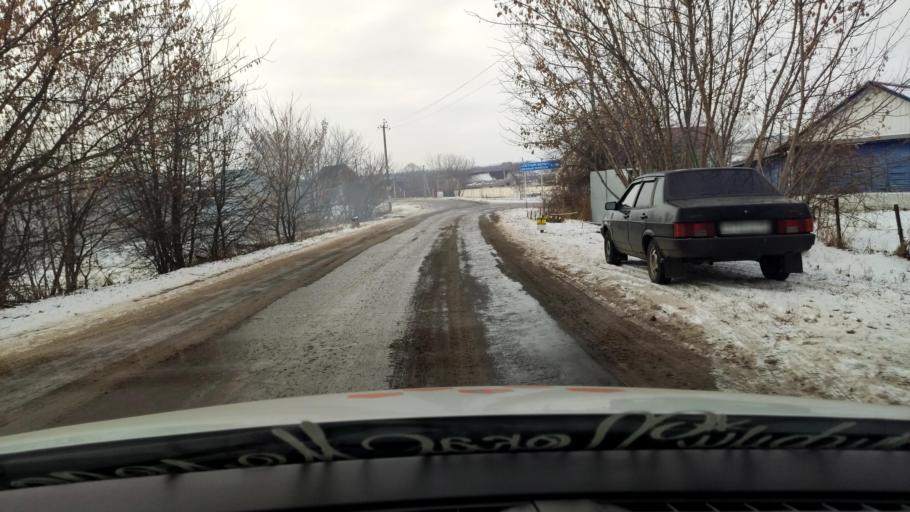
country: RU
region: Voronezj
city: Semiluki
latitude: 51.7494
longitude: 39.0284
